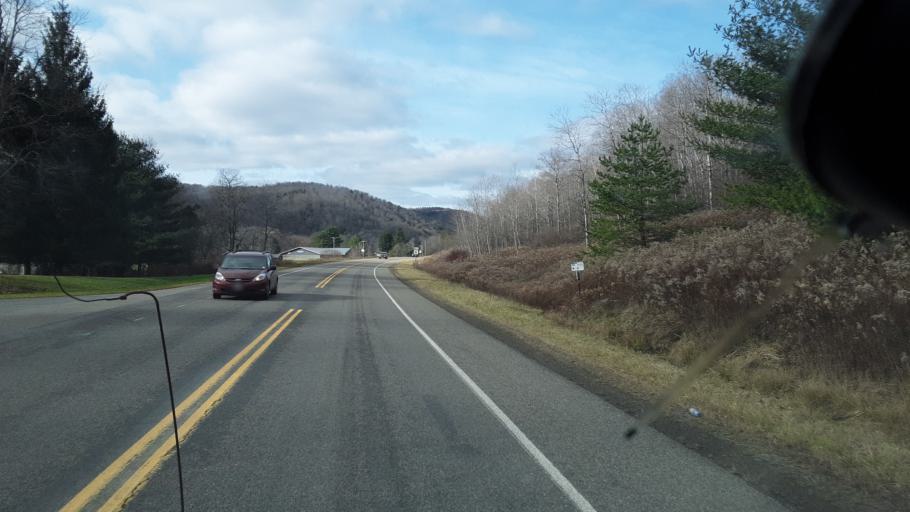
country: US
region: Pennsylvania
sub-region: Potter County
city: Galeton
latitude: 41.7774
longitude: -77.7209
